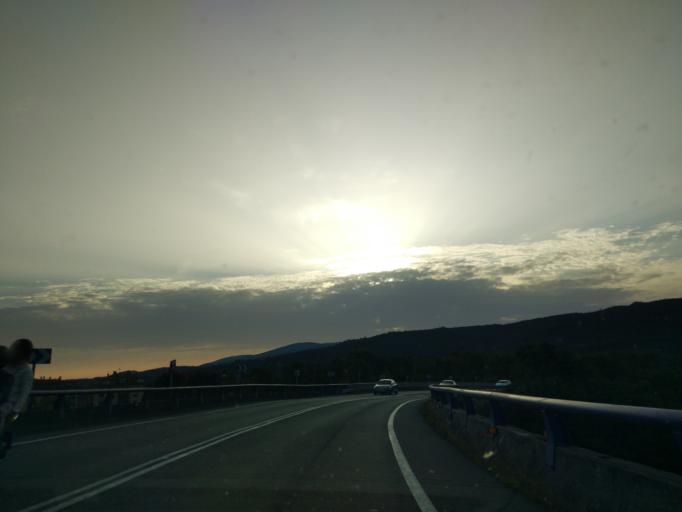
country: ES
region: Galicia
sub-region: Provincia da Coruna
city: Padron
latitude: 42.7293
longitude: -8.6534
